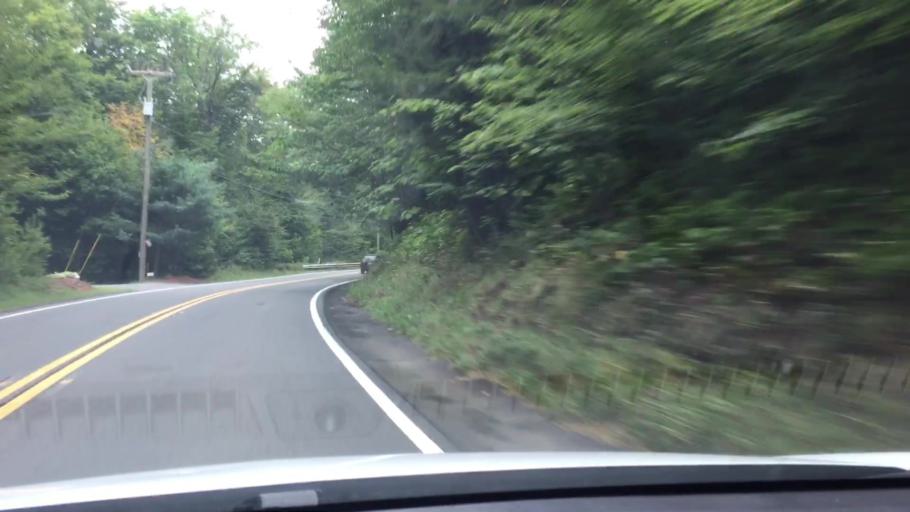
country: US
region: Massachusetts
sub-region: Berkshire County
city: Becket
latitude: 42.3763
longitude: -73.1187
